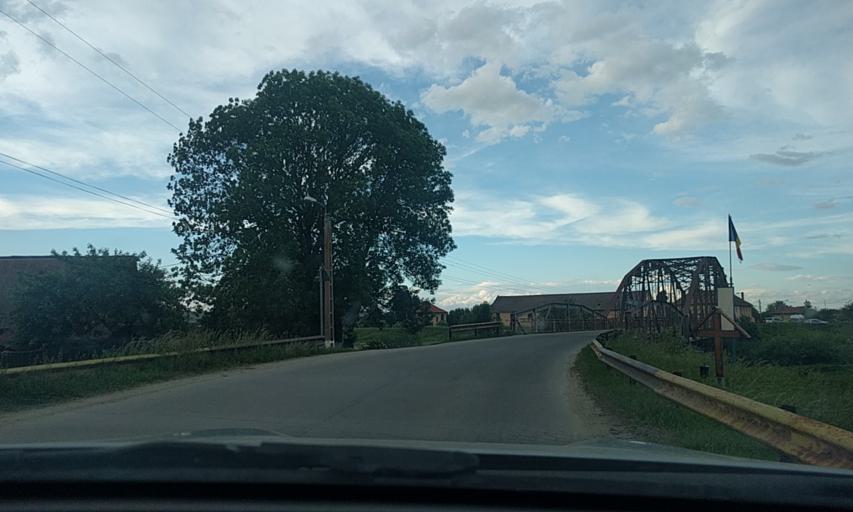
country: RO
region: Brasov
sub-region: Comuna Harman
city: Harman
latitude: 45.7542
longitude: 25.7133
